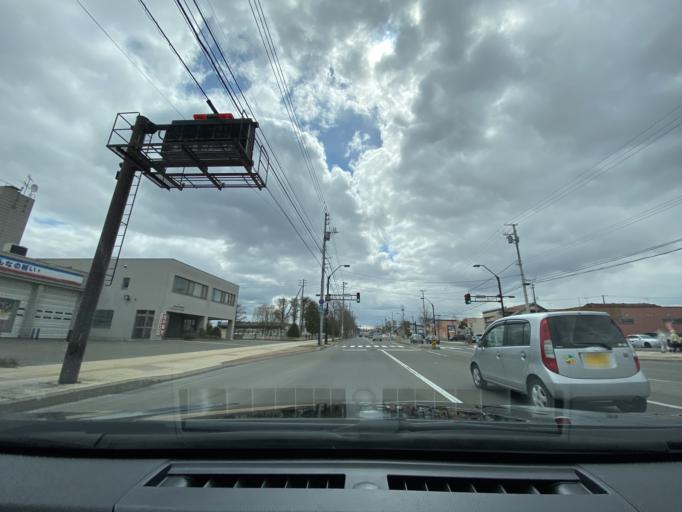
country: JP
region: Hokkaido
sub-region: Asahikawa-shi
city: Asahikawa
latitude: 43.7580
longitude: 142.3491
